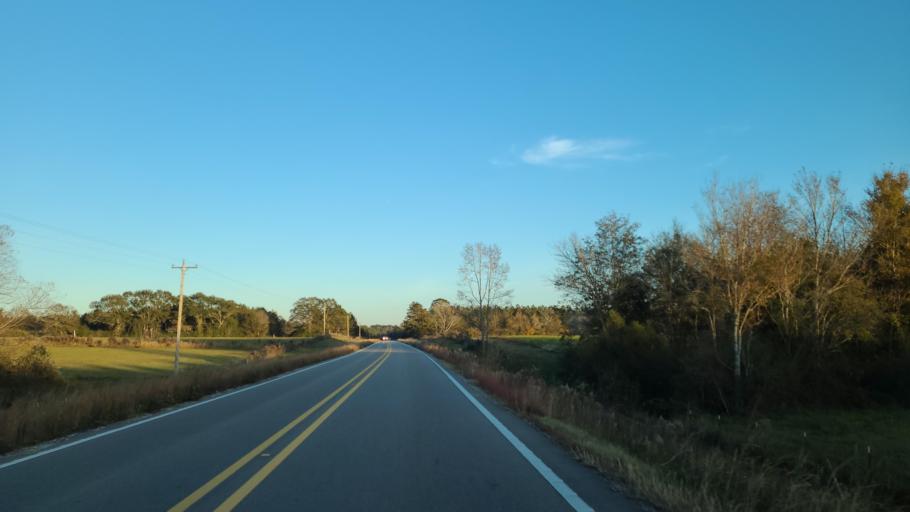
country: US
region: Mississippi
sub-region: Lamar County
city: Lumberton
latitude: 30.9923
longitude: -89.2810
